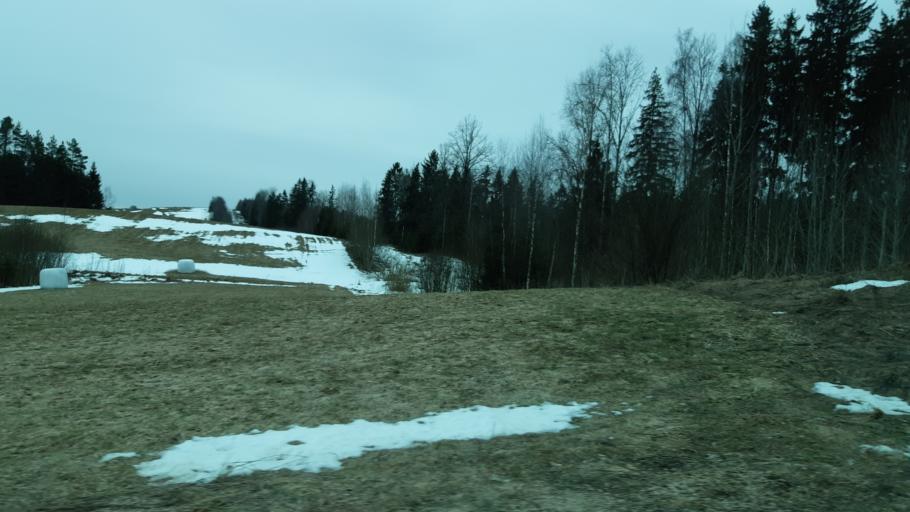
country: LT
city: Virbalis
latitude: 54.3797
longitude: 22.8171
